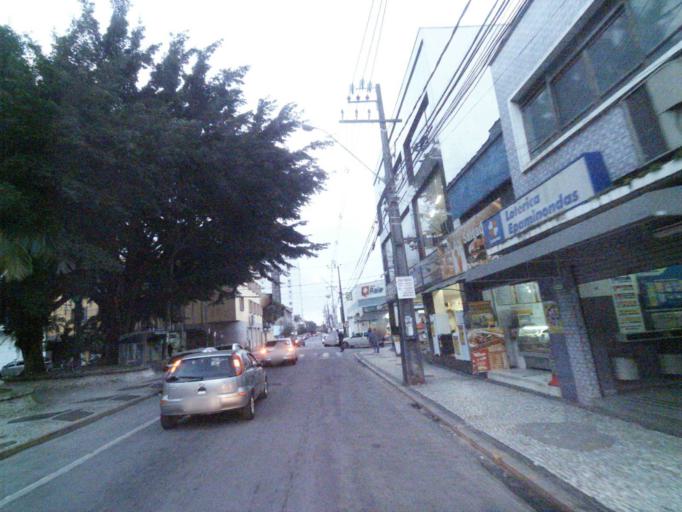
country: BR
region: Parana
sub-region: Paranagua
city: Paranagua
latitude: -25.5184
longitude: -48.5056
